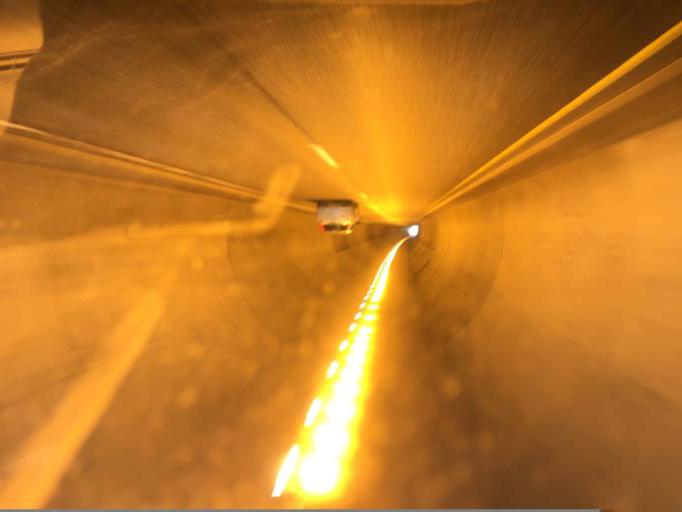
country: NO
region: Vestfold
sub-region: Larvik
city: Larvik
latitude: 59.0661
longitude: 9.9561
